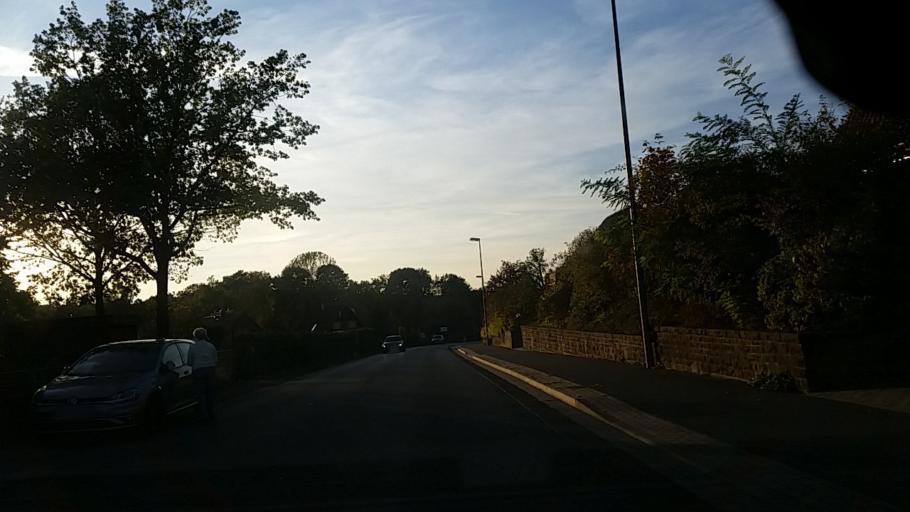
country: DE
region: Lower Saxony
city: Wolfsburg
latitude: 52.4196
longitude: 10.8432
